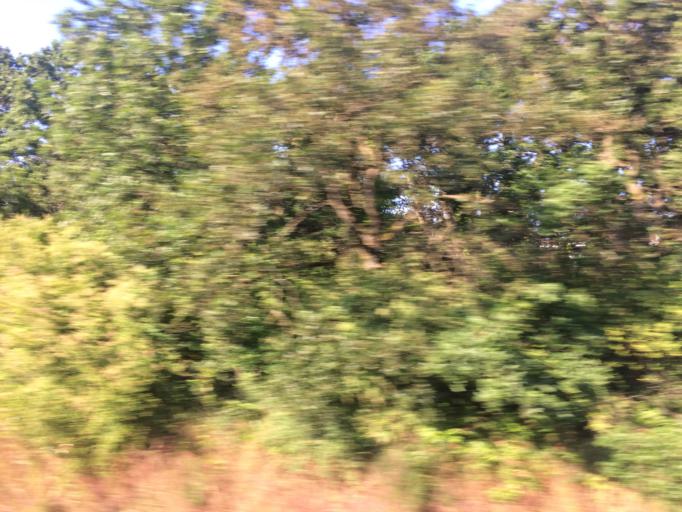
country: CA
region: British Columbia
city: Victoria
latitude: 48.4613
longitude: -123.4104
